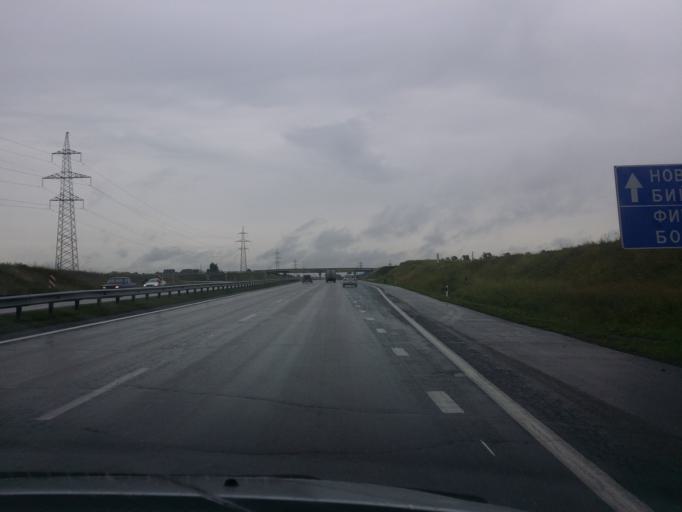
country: RU
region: Altai Krai
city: Sannikovo
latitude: 53.3380
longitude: 83.9326
